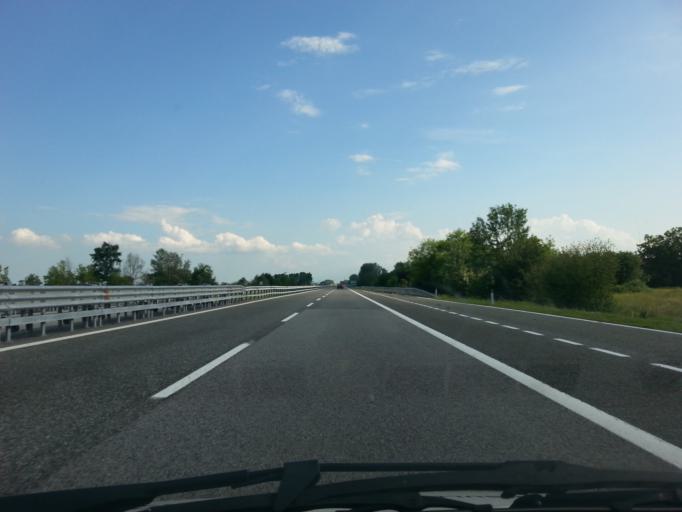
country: IT
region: Piedmont
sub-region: Provincia di Cuneo
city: Sanfre
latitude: 44.7136
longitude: 7.7603
